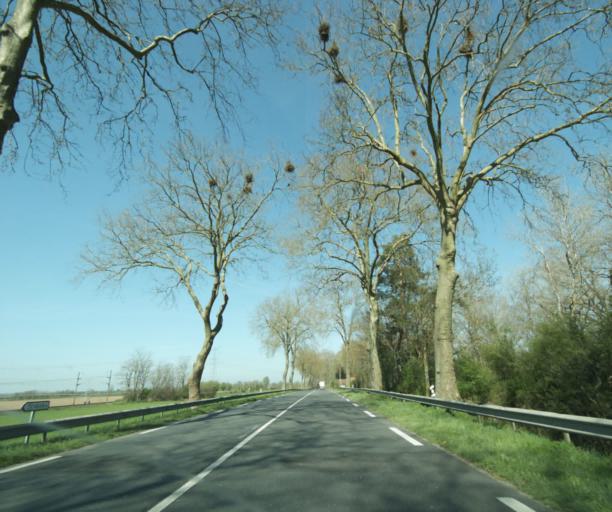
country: FR
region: Bourgogne
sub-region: Departement de la Nievre
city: Chantenay-Saint-Imbert
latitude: 46.6882
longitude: 3.2187
